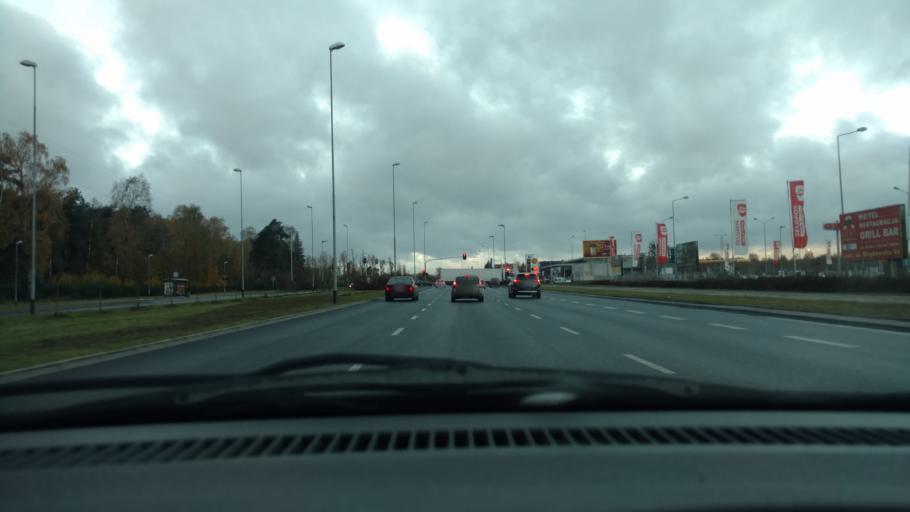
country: PL
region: Lodz Voivodeship
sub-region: Powiat lodzki wschodni
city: Andrespol
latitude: 51.7522
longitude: 19.5846
